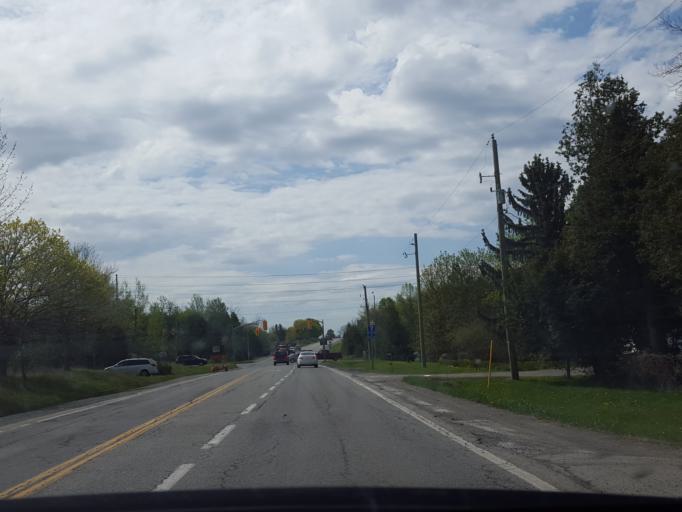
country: CA
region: Ontario
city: Oshawa
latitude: 43.9692
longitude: -78.7280
